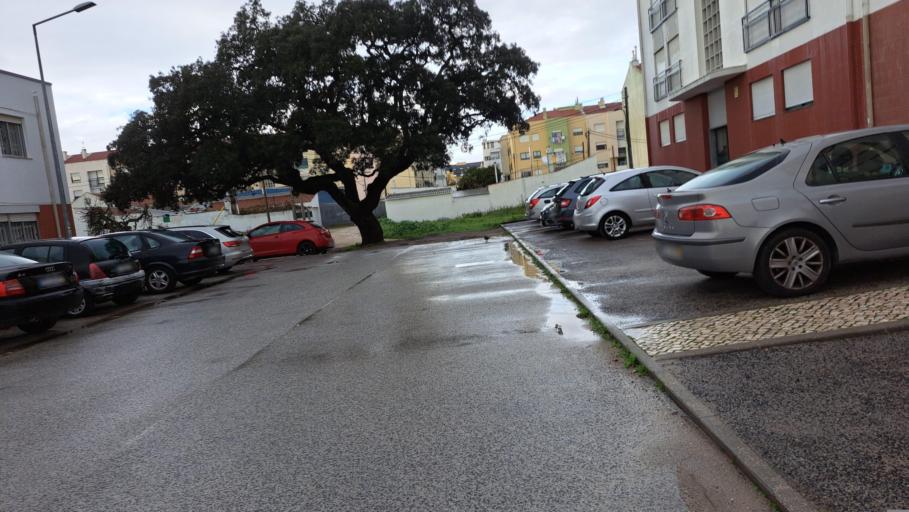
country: PT
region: Setubal
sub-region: Moita
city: Alhos Vedros
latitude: 38.6525
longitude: -9.0395
